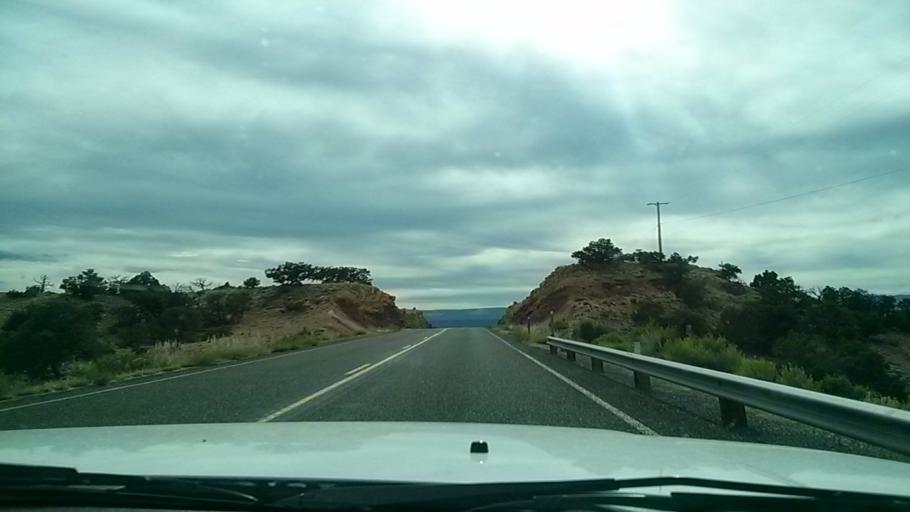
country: US
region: Utah
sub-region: Wayne County
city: Loa
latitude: 37.7507
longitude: -111.4652
